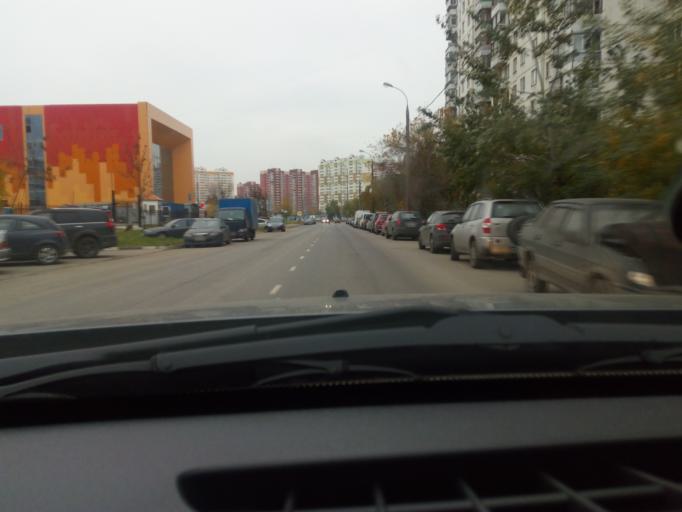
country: RU
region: Moskovskaya
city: Reutov
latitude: 55.7462
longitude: 37.8785
